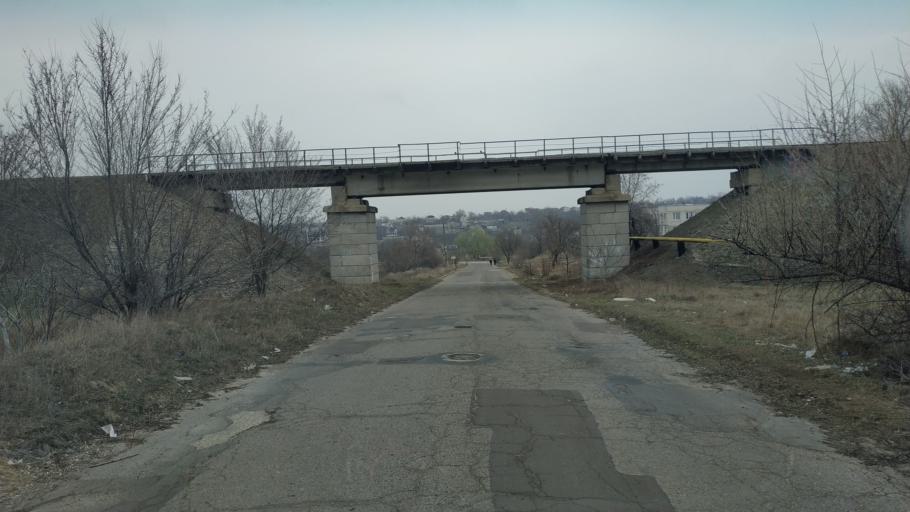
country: MD
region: Chisinau
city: Singera
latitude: 46.9160
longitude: 29.0068
